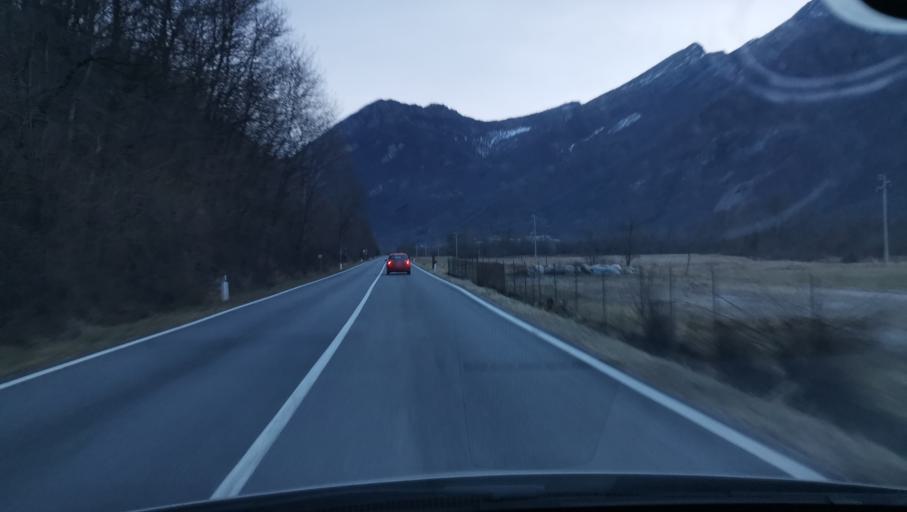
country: IT
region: Piedmont
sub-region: Provincia di Cuneo
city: Valloriate
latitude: 44.3112
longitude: 7.3568
